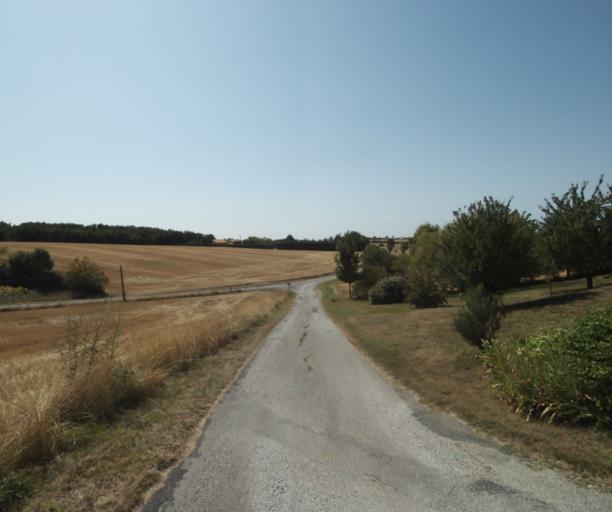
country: FR
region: Midi-Pyrenees
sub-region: Departement de la Haute-Garonne
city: Saint-Felix-Lauragais
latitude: 43.4580
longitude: 1.8541
